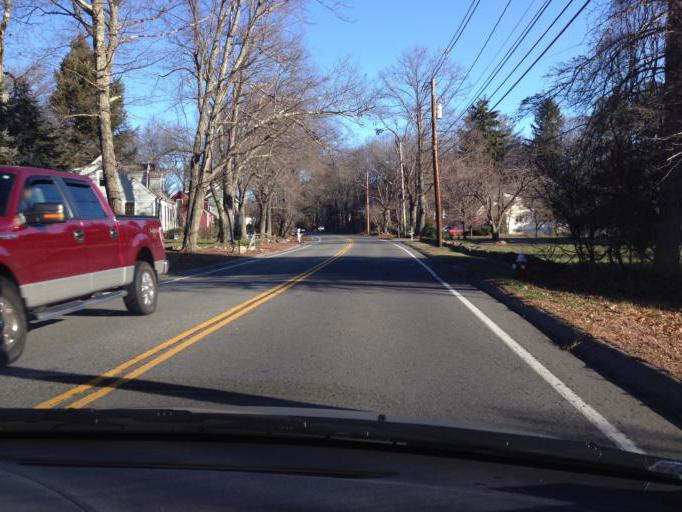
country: US
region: Massachusetts
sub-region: Middlesex County
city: Bedford
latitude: 42.5221
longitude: -71.2870
